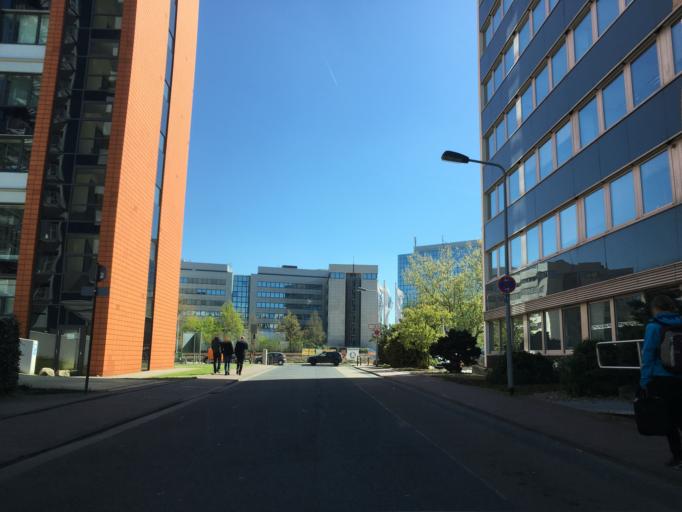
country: DE
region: Hesse
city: Niederrad
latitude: 50.0817
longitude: 8.6327
